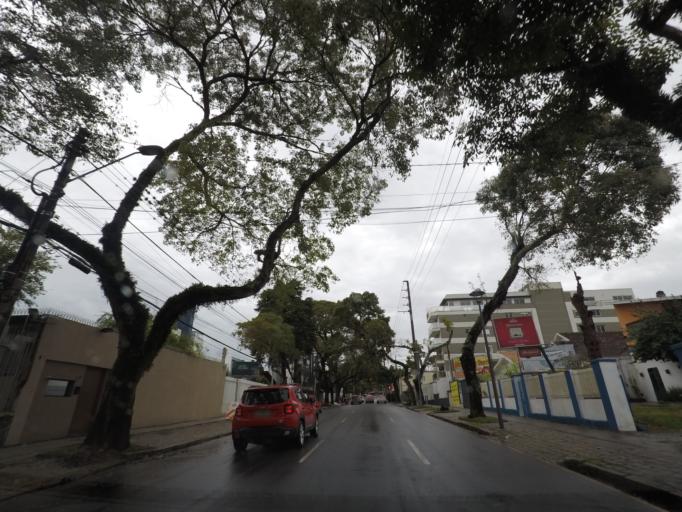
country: BR
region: Parana
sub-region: Curitiba
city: Curitiba
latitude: -25.4499
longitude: -49.2794
